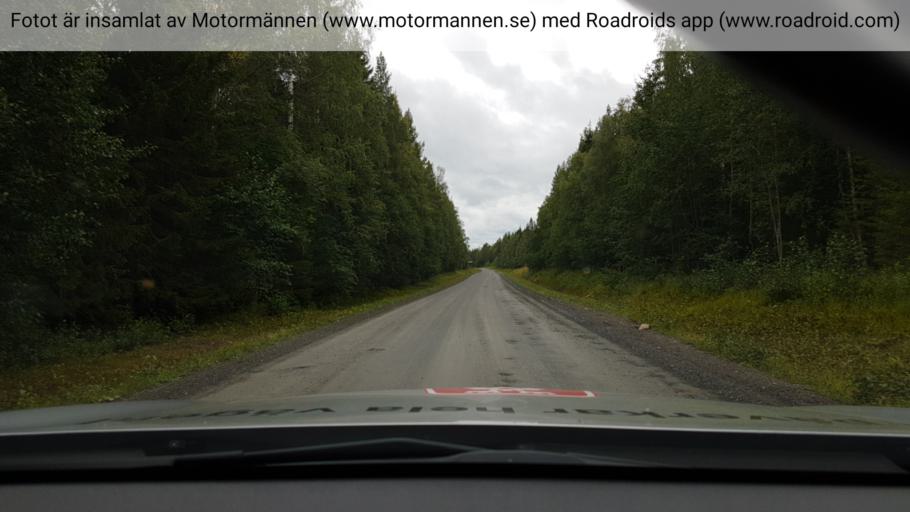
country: SE
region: Vaesterbotten
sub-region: Skelleftea Kommun
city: Forsbacka
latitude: 64.8308
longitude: 20.5009
